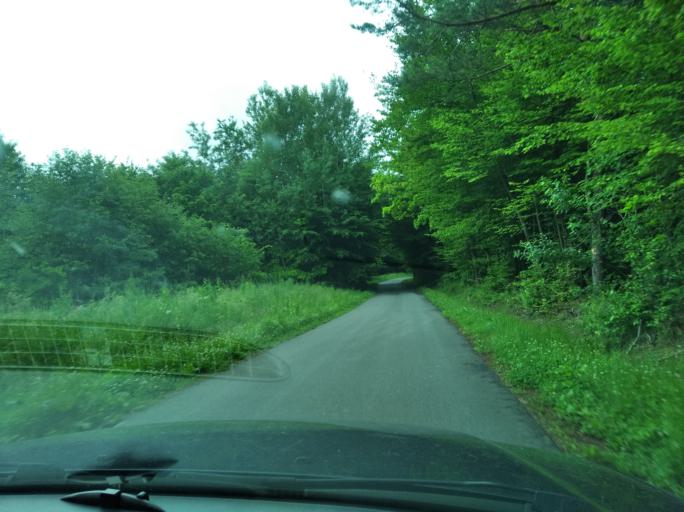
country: PL
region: Subcarpathian Voivodeship
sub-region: Powiat przemyski
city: Dubiecko
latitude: 49.8729
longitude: 22.4050
